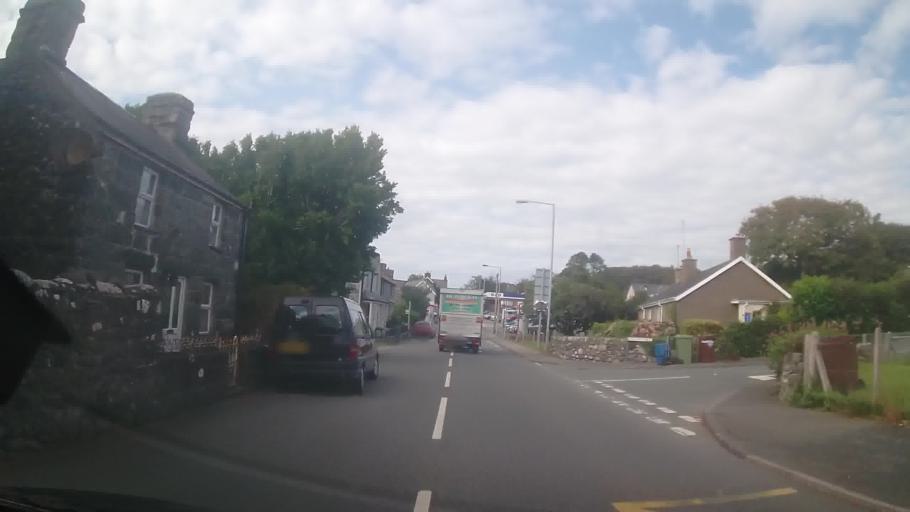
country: GB
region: Wales
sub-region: Gwynedd
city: Llanbedr
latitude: 52.7847
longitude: -4.0963
